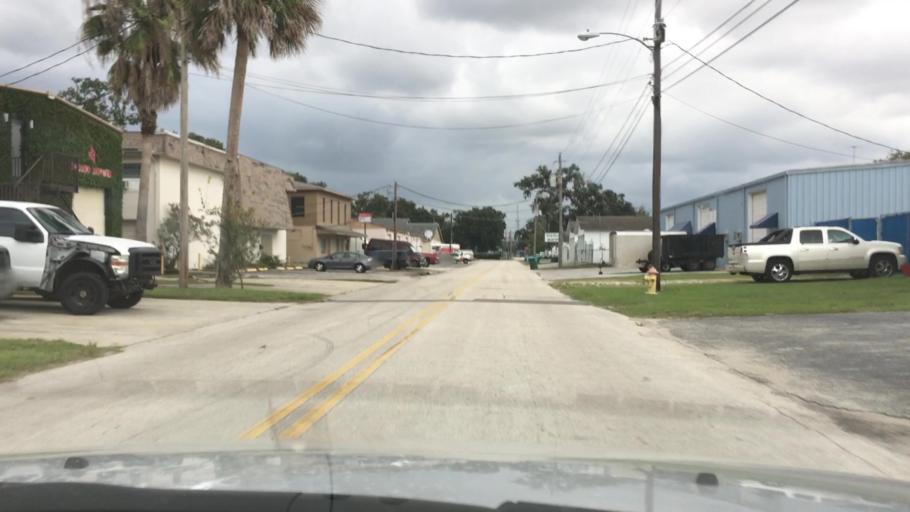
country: US
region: Florida
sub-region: Volusia County
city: Holly Hill
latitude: 29.2401
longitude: -81.0410
